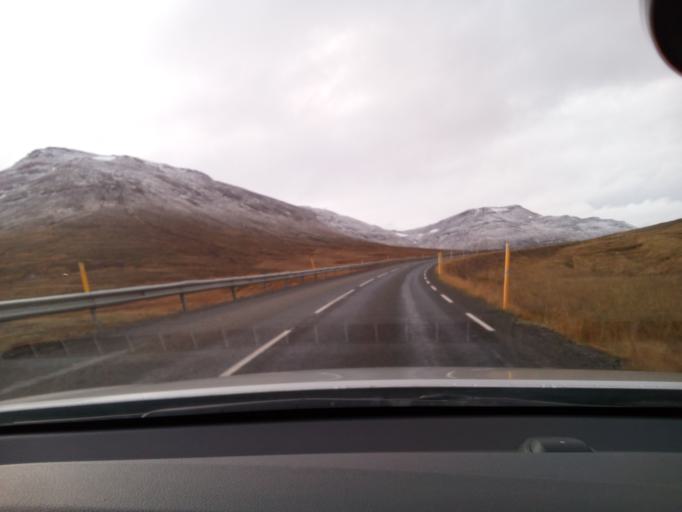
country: IS
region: Northeast
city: Dalvik
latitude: 65.4727
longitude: -18.6719
